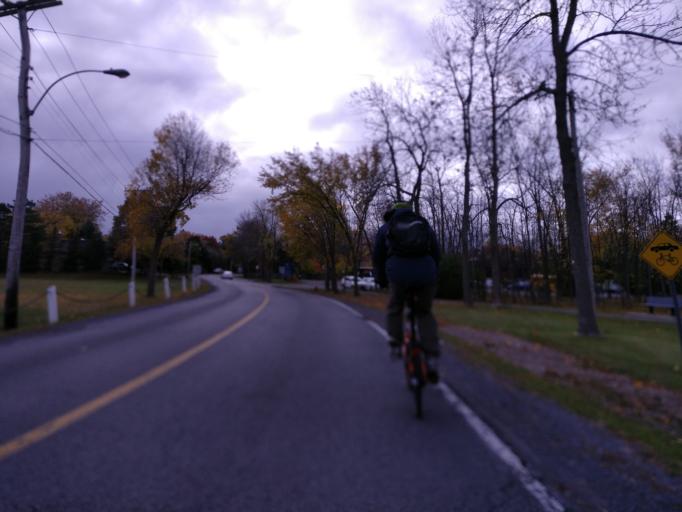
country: CA
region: Quebec
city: Baie-D'Urfe
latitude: 45.4076
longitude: -73.9196
